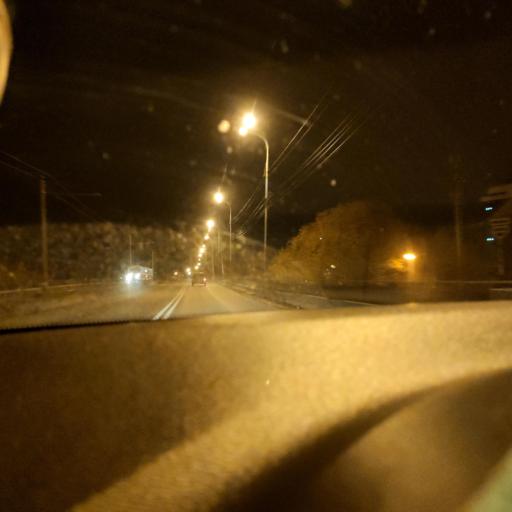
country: RU
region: Samara
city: Smyshlyayevka
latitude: 53.2189
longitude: 50.2904
